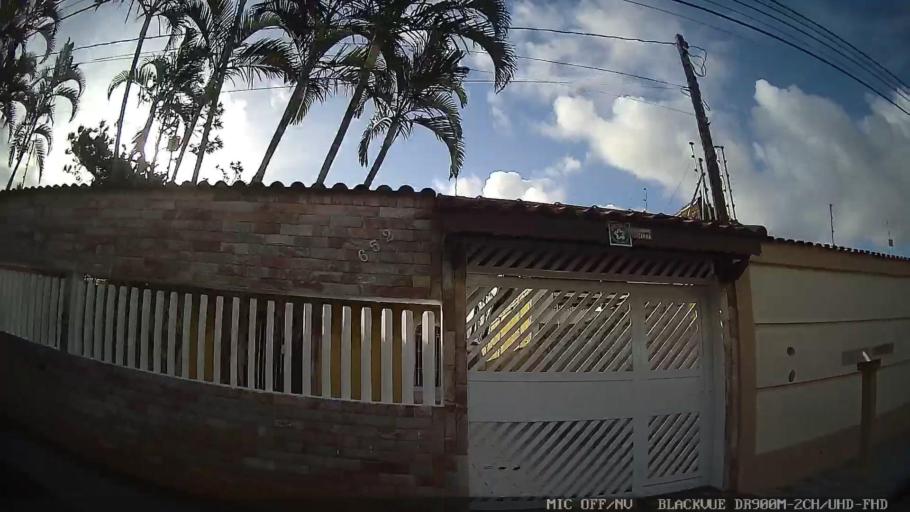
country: BR
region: Sao Paulo
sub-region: Itanhaem
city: Itanhaem
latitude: -24.2044
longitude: -46.8287
